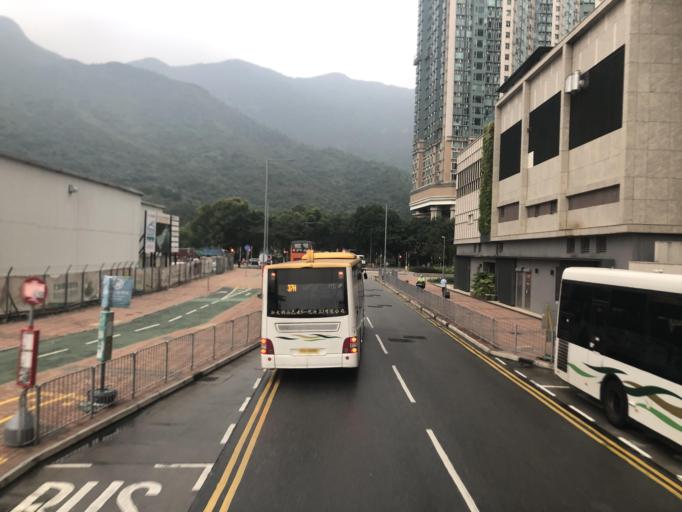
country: HK
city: Tai O
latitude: 22.2957
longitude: 113.9520
